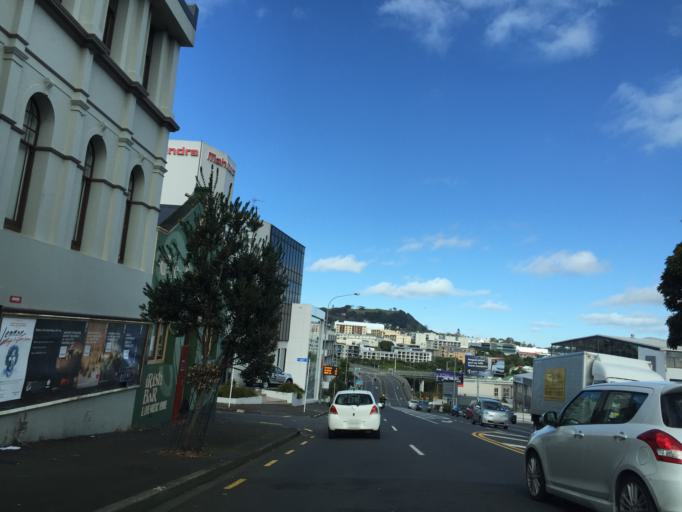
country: NZ
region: Auckland
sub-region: Auckland
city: Auckland
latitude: -36.8598
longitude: 174.7529
